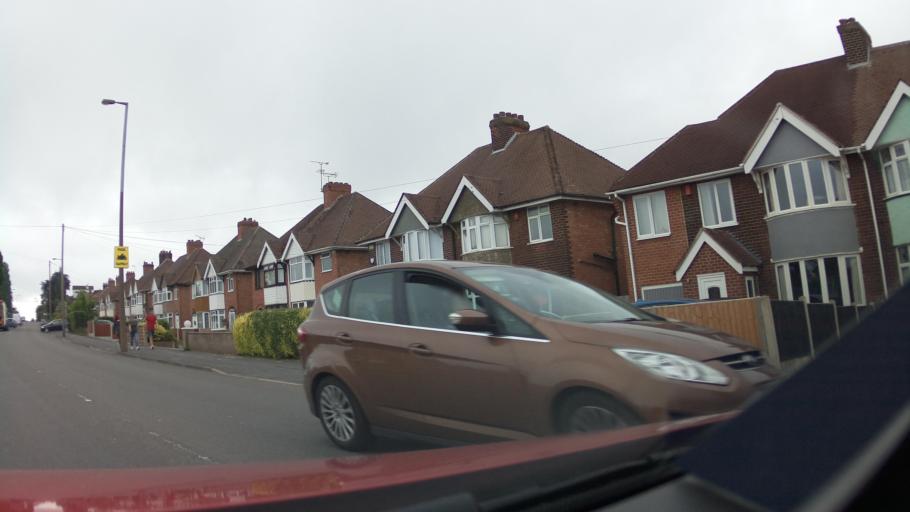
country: GB
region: England
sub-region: Staffordshire
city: Burton upon Trent
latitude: 52.7858
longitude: -1.6165
